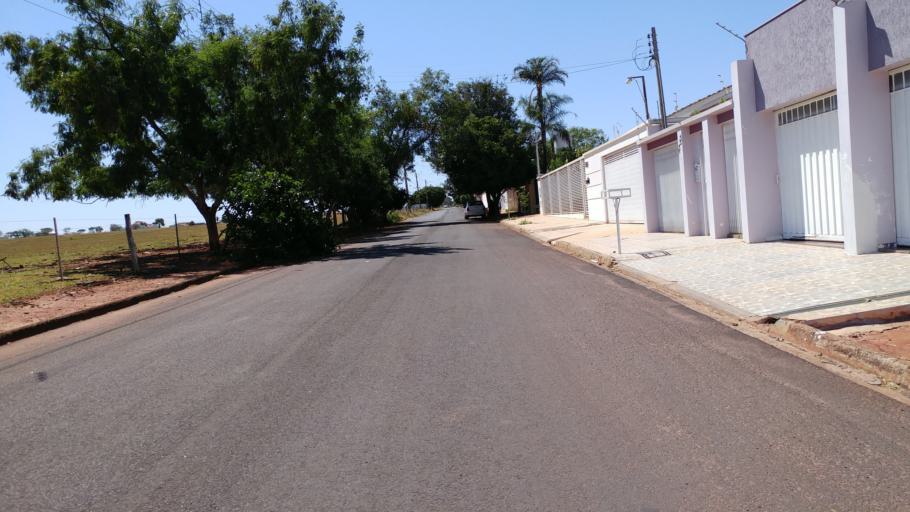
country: BR
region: Sao Paulo
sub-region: Paraguacu Paulista
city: Paraguacu Paulista
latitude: -22.4090
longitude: -50.5898
